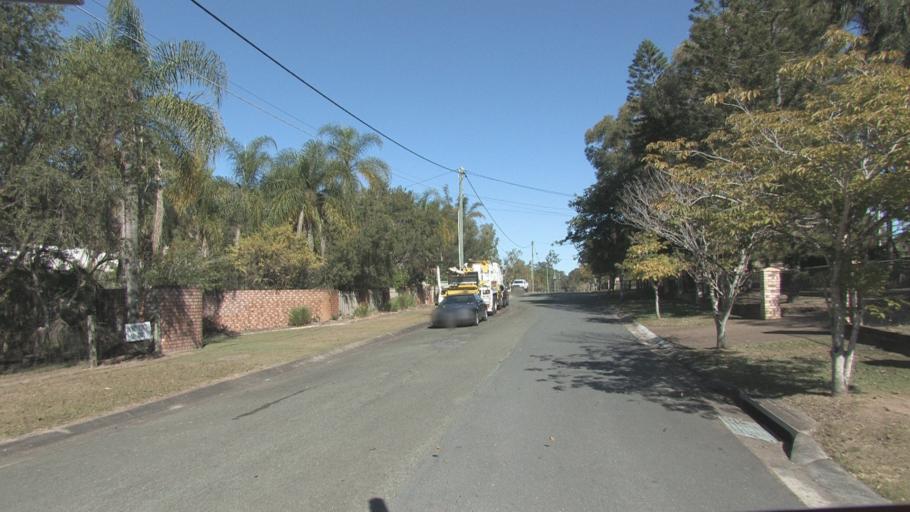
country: AU
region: Queensland
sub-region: Logan
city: Logan Reserve
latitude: -27.7030
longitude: 153.0708
